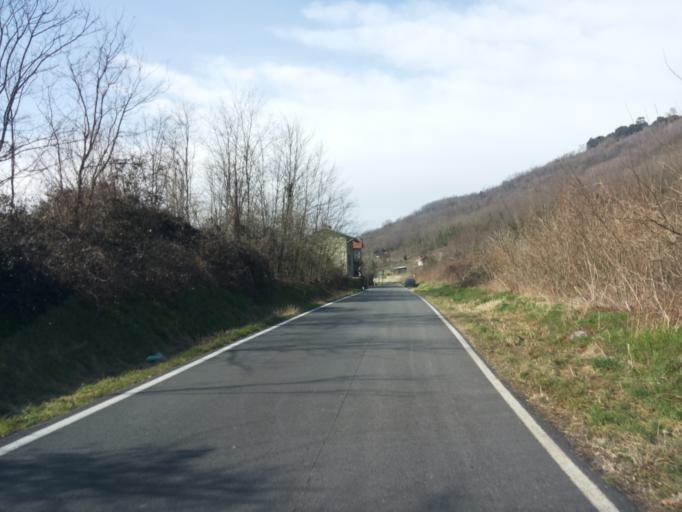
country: IT
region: Piedmont
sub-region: Provincia di Torino
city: Vestigne
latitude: 45.3818
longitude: 7.9640
